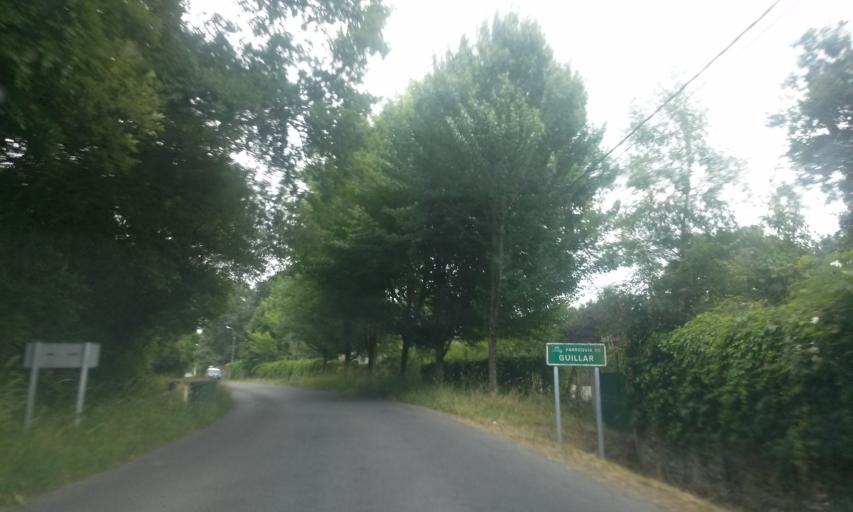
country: ES
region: Galicia
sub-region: Provincia de Lugo
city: Outeiro de Rei
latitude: 43.0729
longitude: -7.6286
